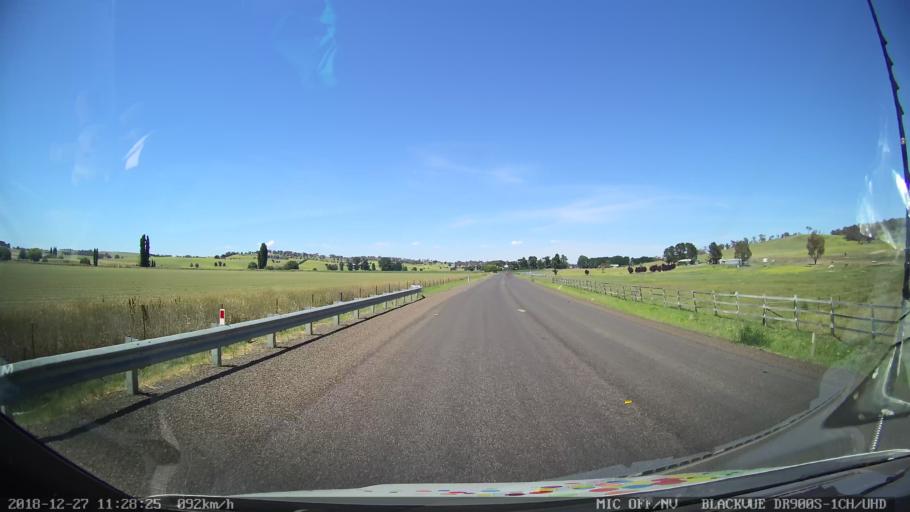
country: AU
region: New South Wales
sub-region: Bathurst Regional
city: Perthville
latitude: -33.4760
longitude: 149.5637
